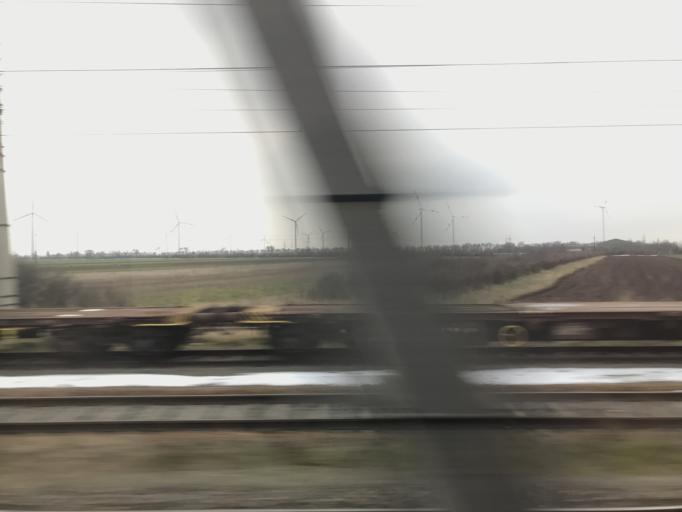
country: AT
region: Burgenland
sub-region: Politischer Bezirk Neusiedl am See
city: Parndorf
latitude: 47.9869
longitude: 16.8744
